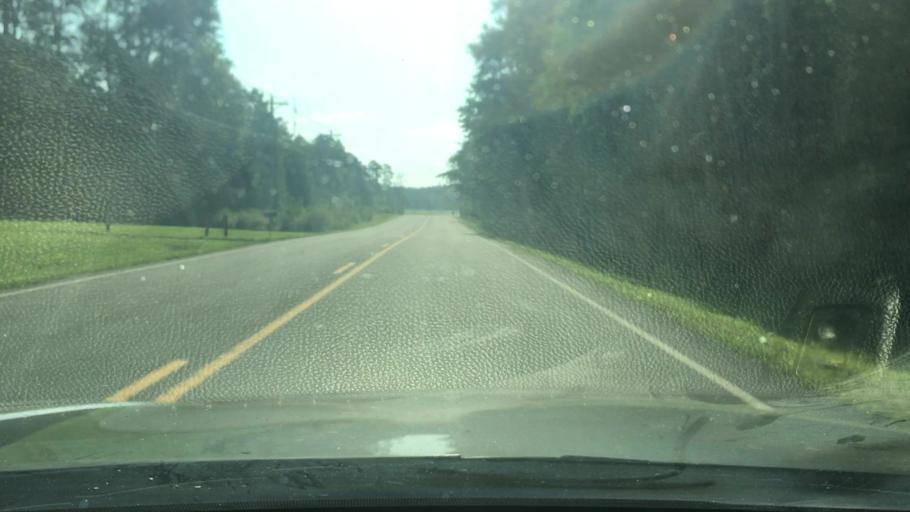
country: US
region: North Carolina
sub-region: Caswell County
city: Yanceyville
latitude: 36.2808
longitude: -79.3545
